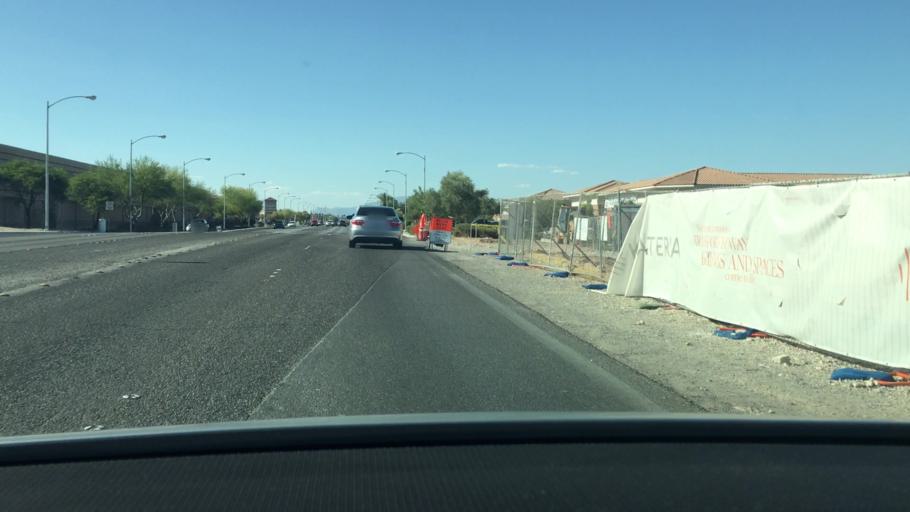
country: US
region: Nevada
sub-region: Clark County
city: Summerlin South
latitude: 36.0866
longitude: -115.2974
